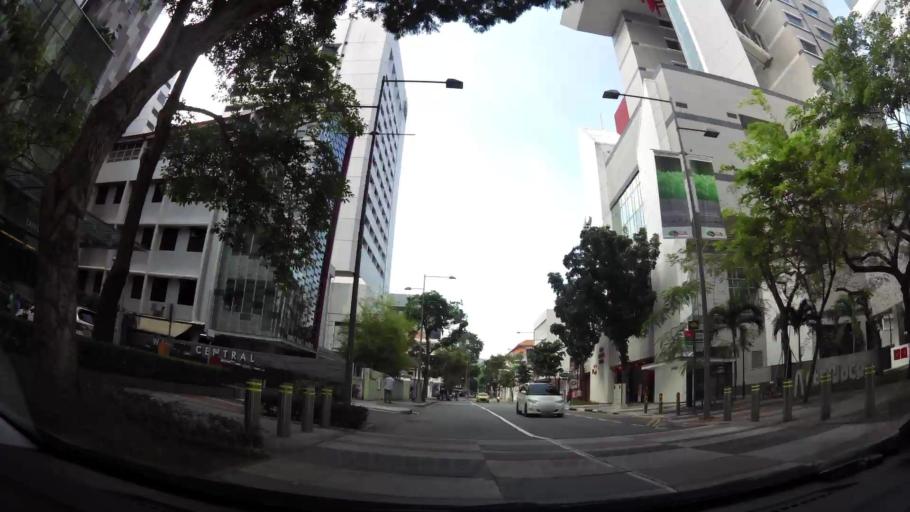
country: SG
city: Singapore
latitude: 1.2982
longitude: 103.8525
